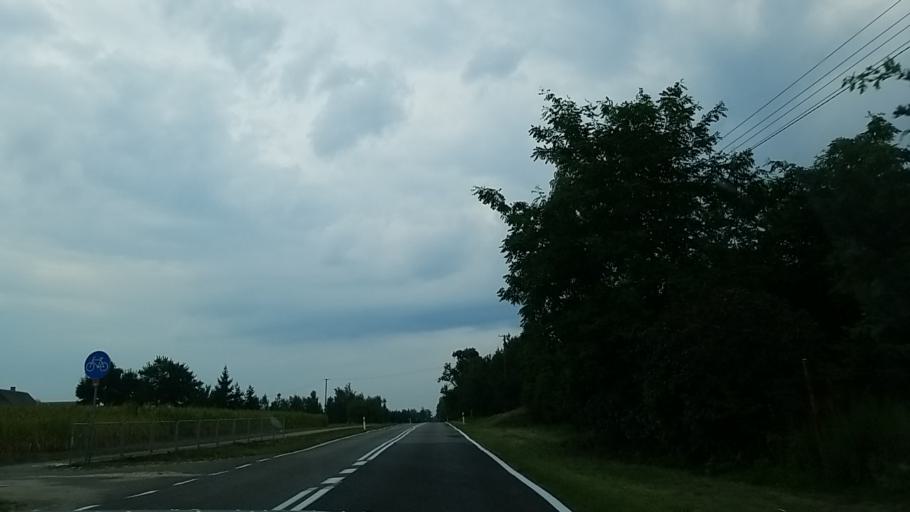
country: PL
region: Lublin Voivodeship
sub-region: Powiat bialski
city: Slawatycze
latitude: 51.7446
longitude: 23.5315
